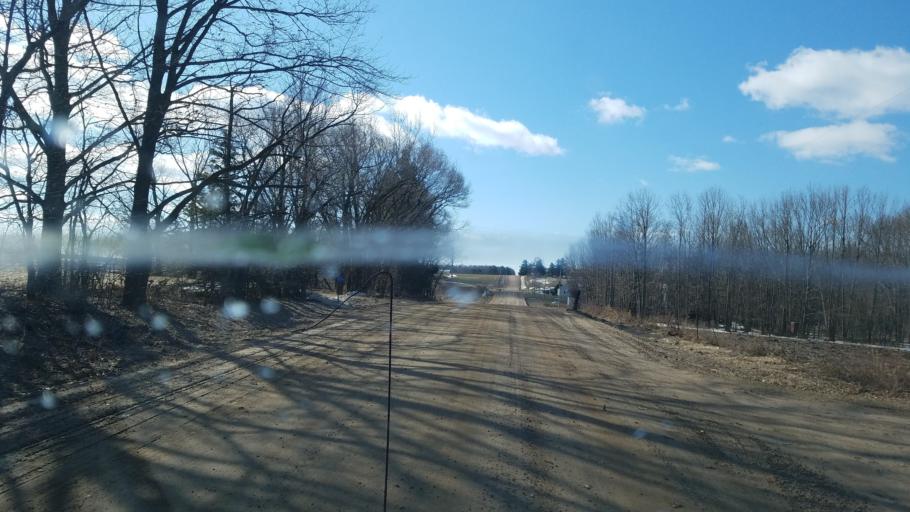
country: US
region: Wisconsin
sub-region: Clark County
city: Loyal
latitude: 44.6737
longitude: -90.4559
